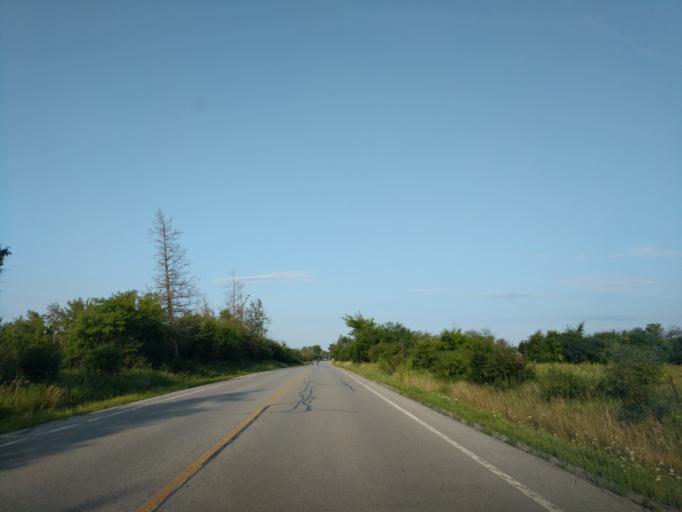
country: CA
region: Ontario
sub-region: York
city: Richmond Hill
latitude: 43.9139
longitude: -79.4109
